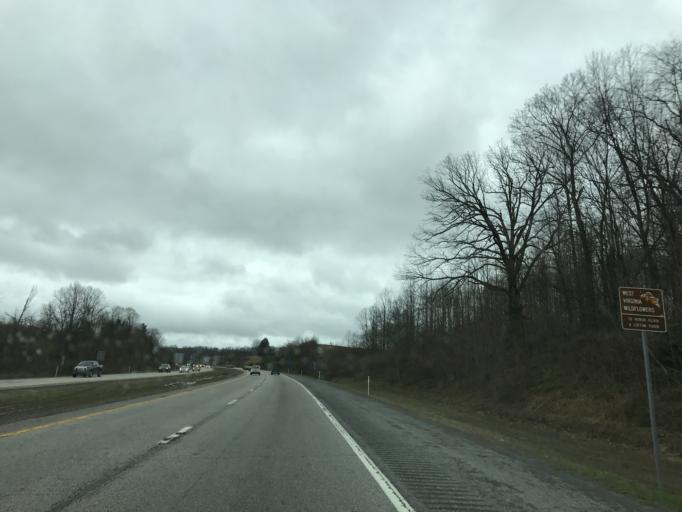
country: US
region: West Virginia
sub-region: Fayette County
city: Fayetteville
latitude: 38.0455
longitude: -81.1217
